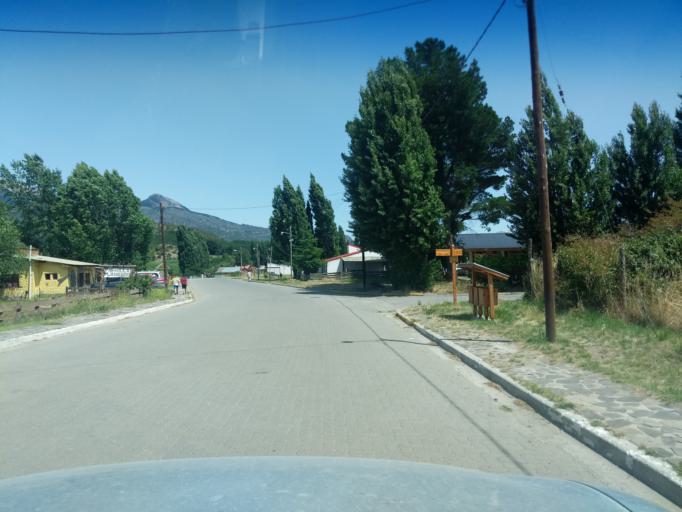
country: CL
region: Los Lagos
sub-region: Provincia de Palena
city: Palena
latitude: -43.5358
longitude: -71.4719
